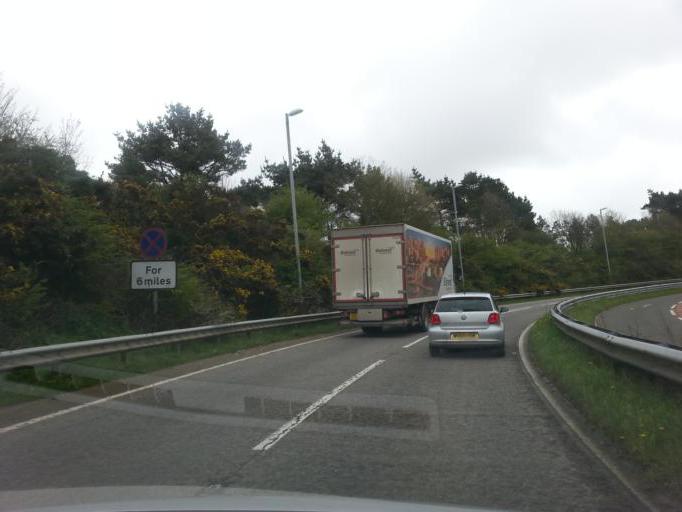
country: GB
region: England
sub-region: Cornwall
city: Camborne
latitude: 50.2305
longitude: -5.2836
